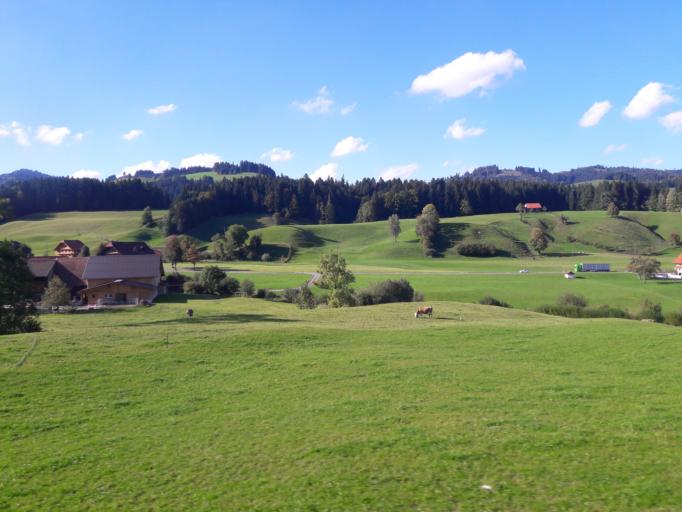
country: CH
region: Lucerne
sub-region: Entlebuch District
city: Escholzmatt
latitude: 46.9280
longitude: 7.9740
